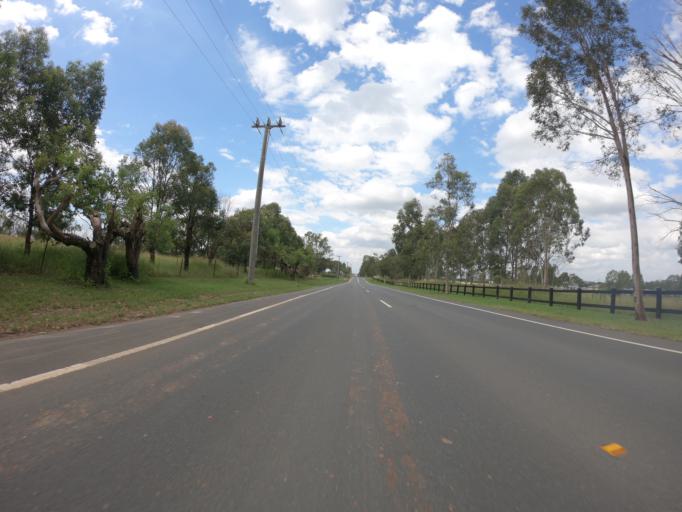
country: AU
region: New South Wales
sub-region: Liverpool
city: Luddenham
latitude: -33.8367
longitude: 150.7505
